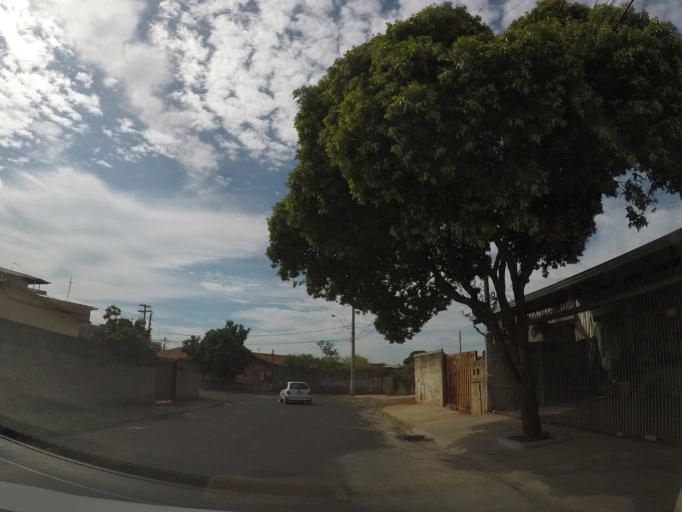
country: BR
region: Sao Paulo
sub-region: Hortolandia
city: Hortolandia
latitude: -22.8345
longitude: -47.1885
